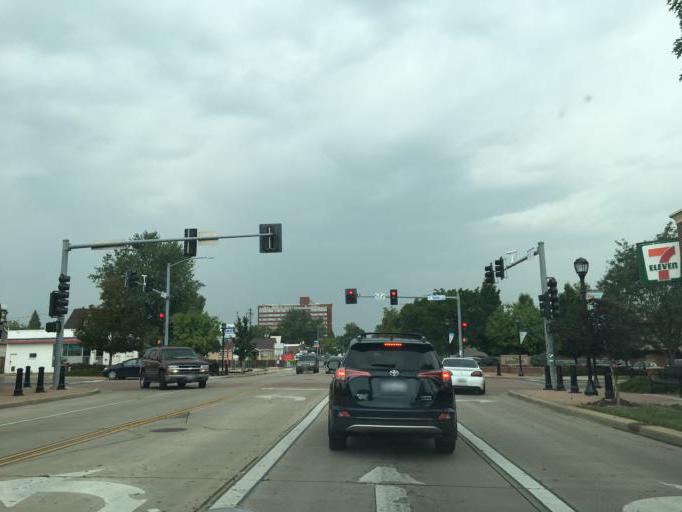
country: US
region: Colorado
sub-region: Jefferson County
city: Wheat Ridge
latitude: 39.7694
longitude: -105.0622
